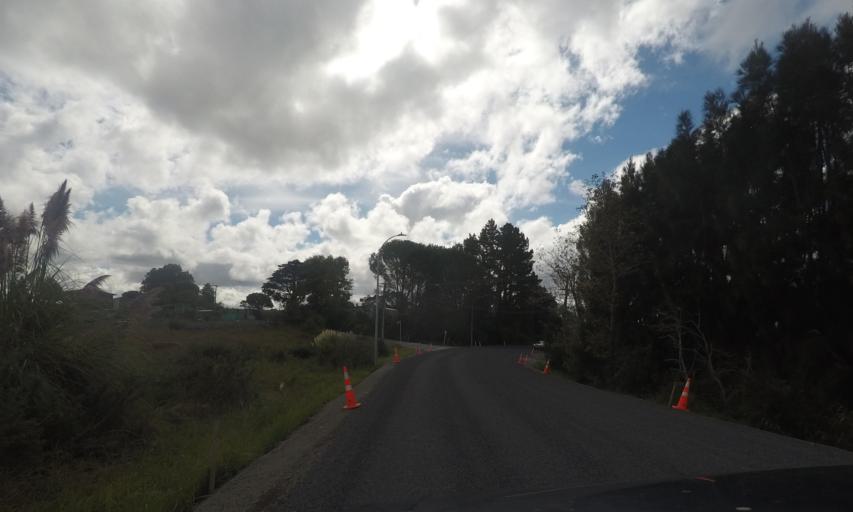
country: NZ
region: Auckland
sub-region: Auckland
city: Rosebank
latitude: -36.7923
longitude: 174.6371
